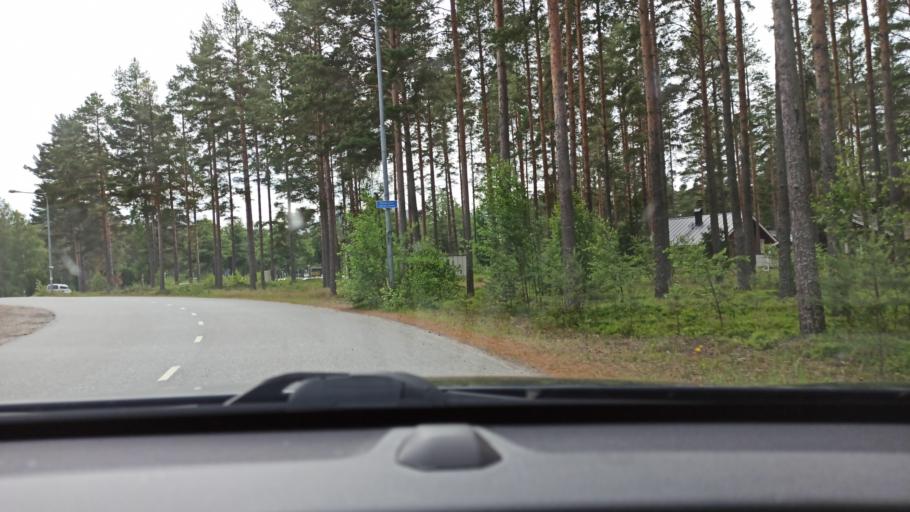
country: FI
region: Satakunta
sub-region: Pori
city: Luvia
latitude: 61.5724
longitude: 21.5200
